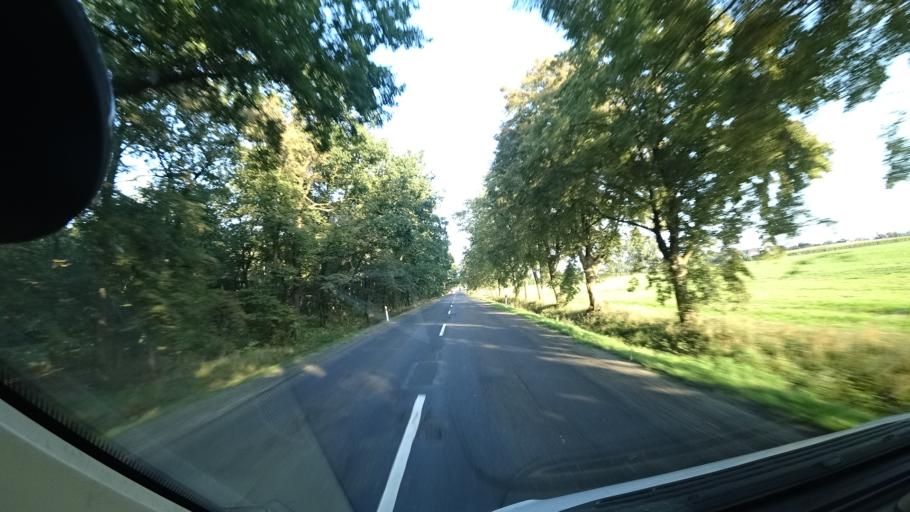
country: PL
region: Opole Voivodeship
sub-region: Powiat kedzierzynsko-kozielski
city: Bierawa
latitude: 50.2942
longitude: 18.2446
